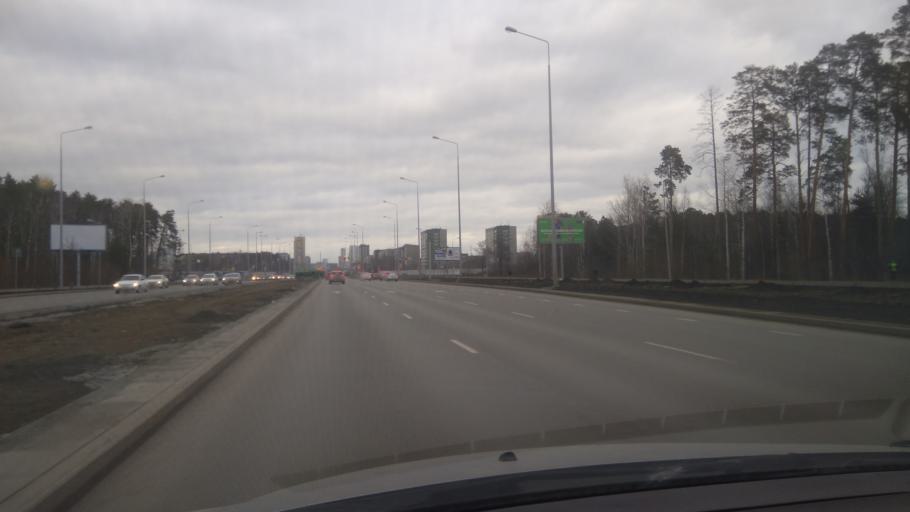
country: RU
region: Sverdlovsk
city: Sovkhoznyy
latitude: 56.8015
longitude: 60.5358
